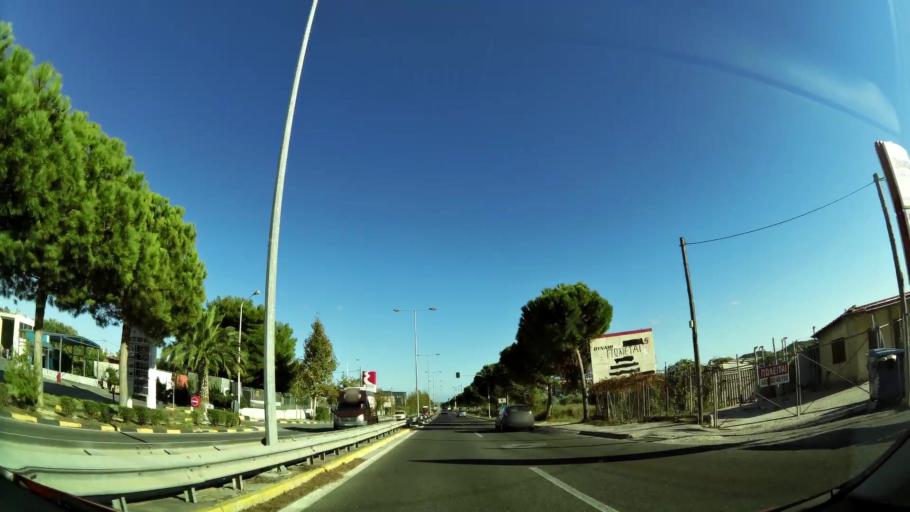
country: GR
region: Attica
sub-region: Nomarchia Anatolikis Attikis
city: Pikermi
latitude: 37.9991
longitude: 23.9163
